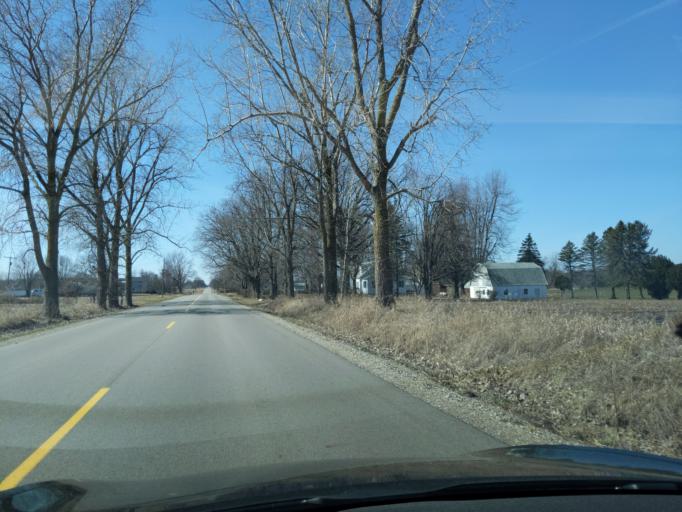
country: US
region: Michigan
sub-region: Eaton County
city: Grand Ledge
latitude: 42.7266
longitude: -84.8222
